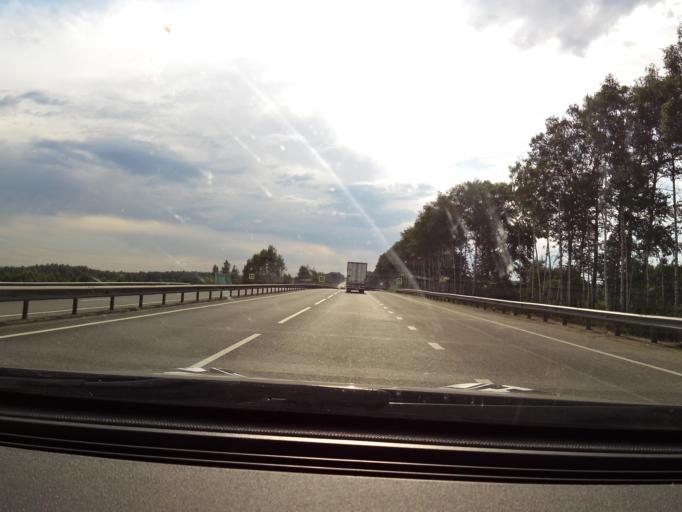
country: RU
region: Vladimir
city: Gorokhovets
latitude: 56.1600
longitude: 42.5592
